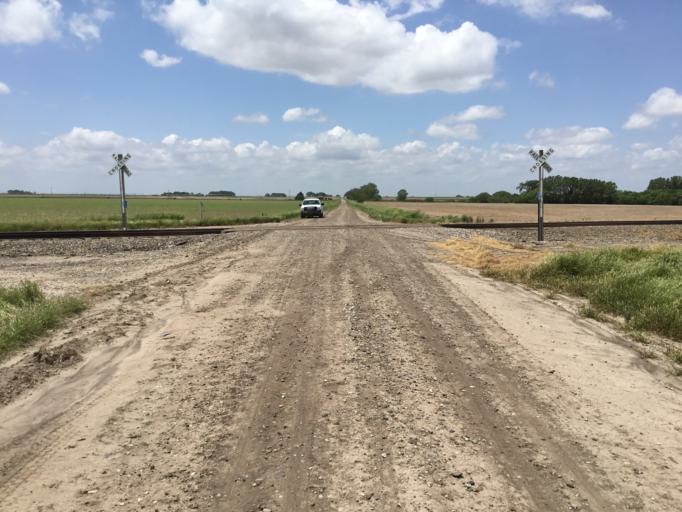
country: US
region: Kansas
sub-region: Republic County
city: Belleville
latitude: 39.7263
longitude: -97.8695
